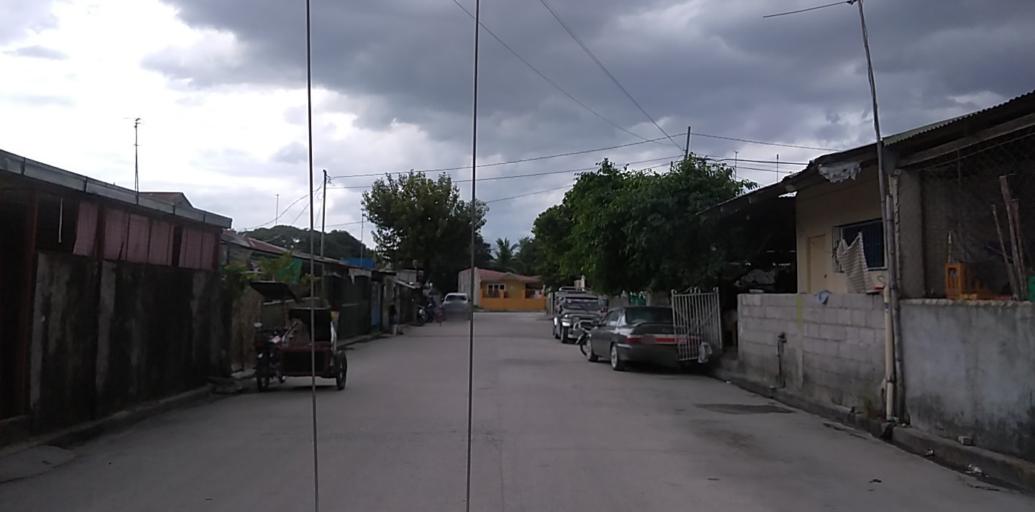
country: PH
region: Central Luzon
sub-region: Province of Pampanga
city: Pio
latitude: 15.0424
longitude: 120.5287
